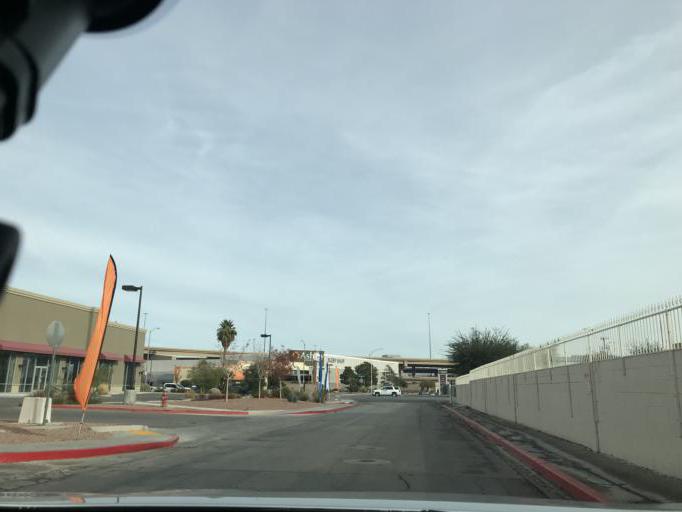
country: US
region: Nevada
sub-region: Clark County
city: Las Vegas
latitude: 36.1734
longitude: -115.1621
